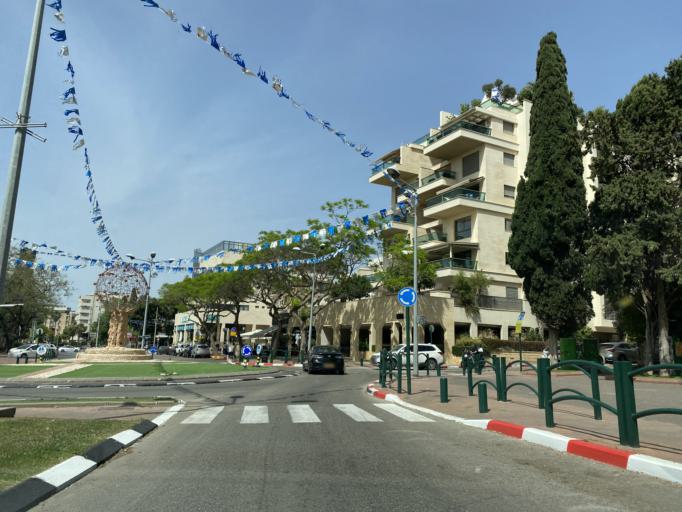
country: IL
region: Central District
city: Ra'anana
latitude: 32.1798
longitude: 34.8716
